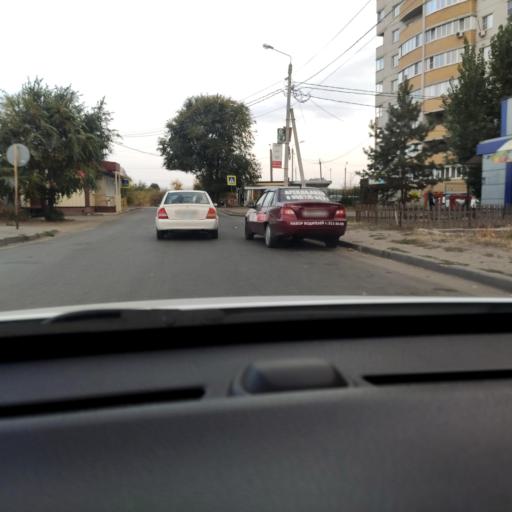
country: RU
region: Voronezj
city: Somovo
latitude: 51.6700
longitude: 39.2907
